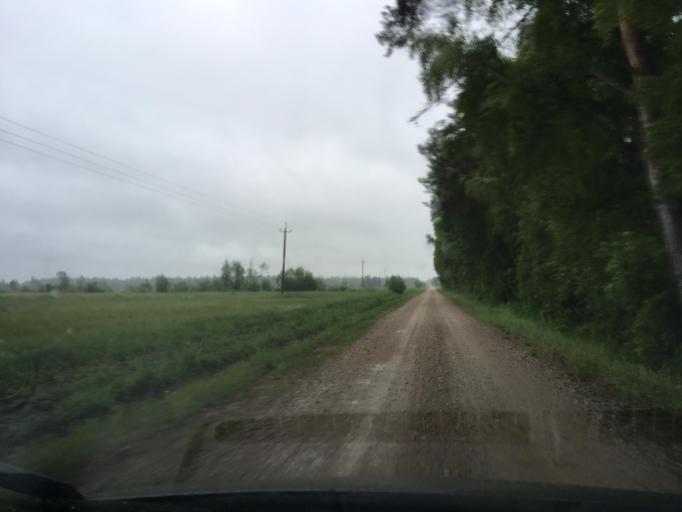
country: EE
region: Laeaene
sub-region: Lihula vald
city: Lihula
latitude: 58.6082
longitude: 23.8281
